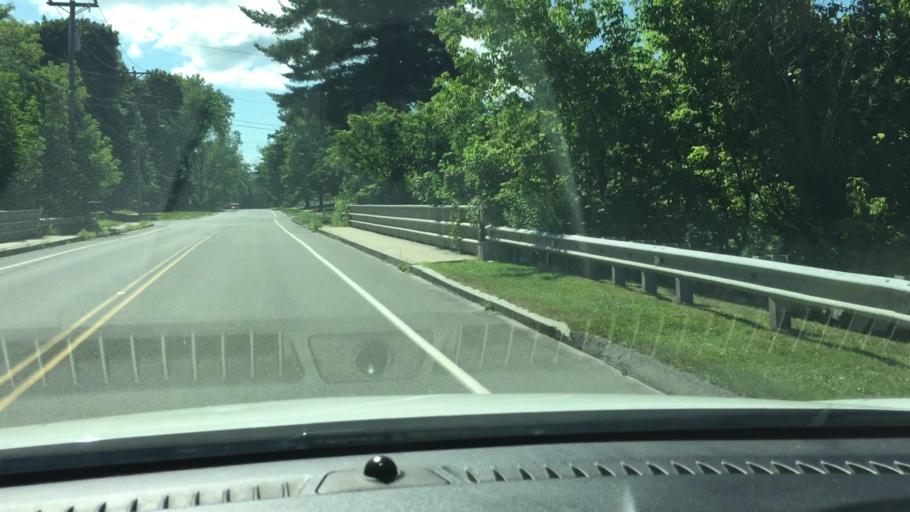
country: US
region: Massachusetts
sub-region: Berkshire County
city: Pittsfield
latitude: 42.4367
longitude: -73.2481
